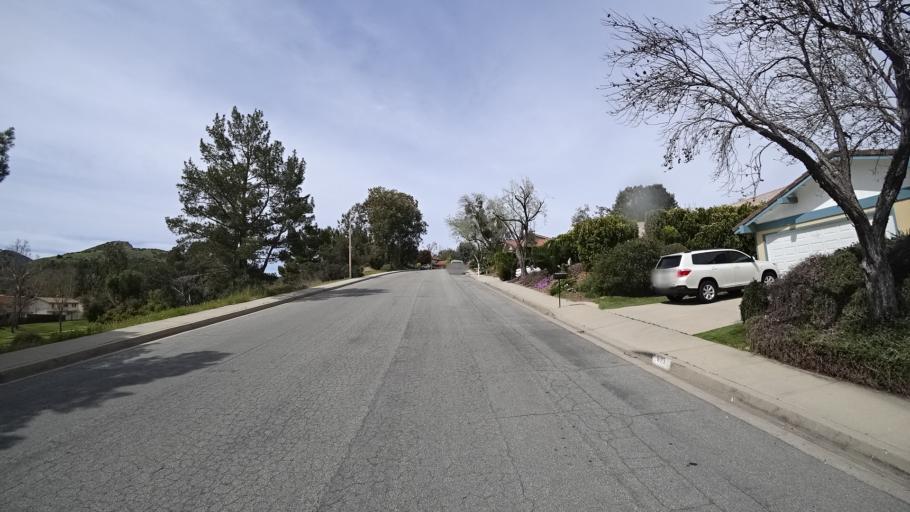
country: US
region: California
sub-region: Ventura County
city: Thousand Oaks
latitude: 34.1475
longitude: -118.8492
